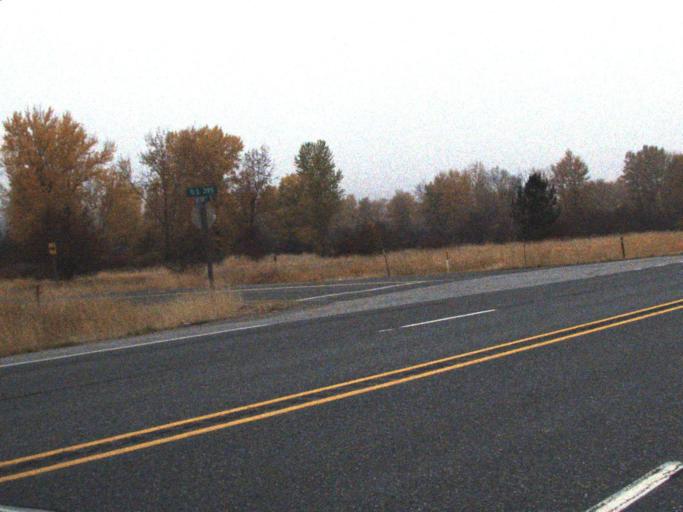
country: US
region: Washington
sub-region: Stevens County
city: Kettle Falls
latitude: 48.5874
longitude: -117.9821
